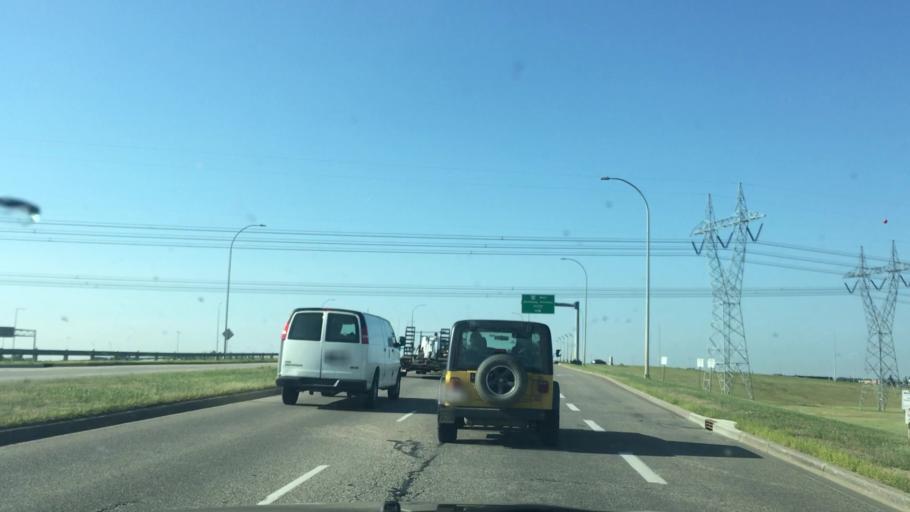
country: CA
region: Alberta
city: Edmonton
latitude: 53.4377
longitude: -113.5187
